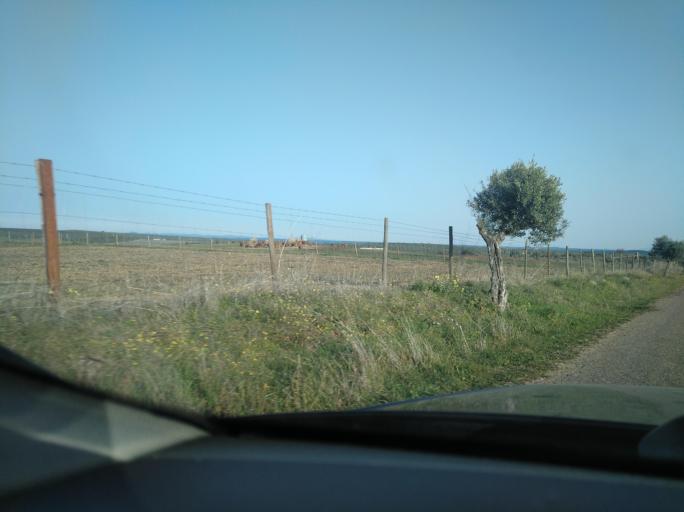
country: PT
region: Portalegre
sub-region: Campo Maior
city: Campo Maior
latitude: 39.0106
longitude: -7.0319
